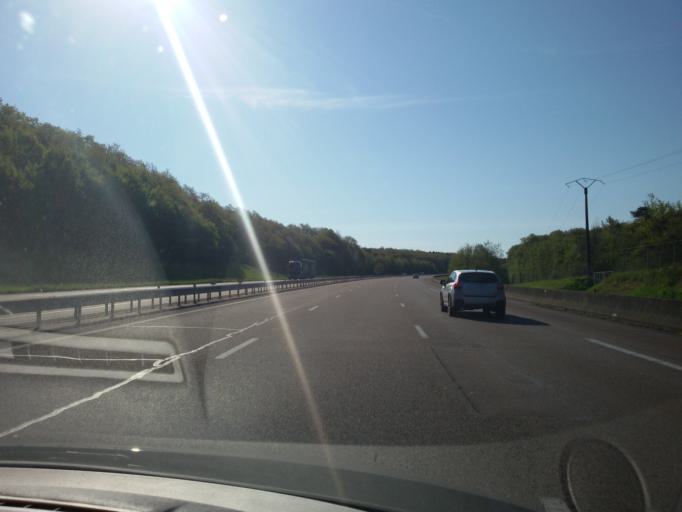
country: FR
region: Bourgogne
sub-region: Departement de l'Yonne
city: Aillant-sur-Tholon
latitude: 47.9249
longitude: 3.2778
